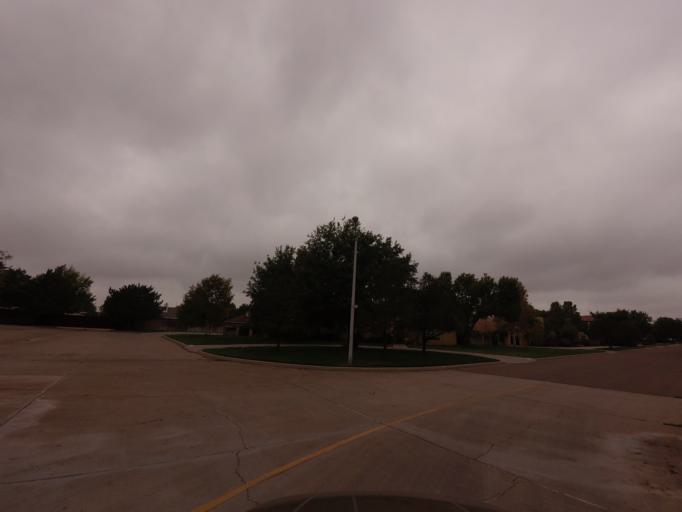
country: US
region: New Mexico
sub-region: Curry County
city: Clovis
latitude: 34.4272
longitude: -103.1826
